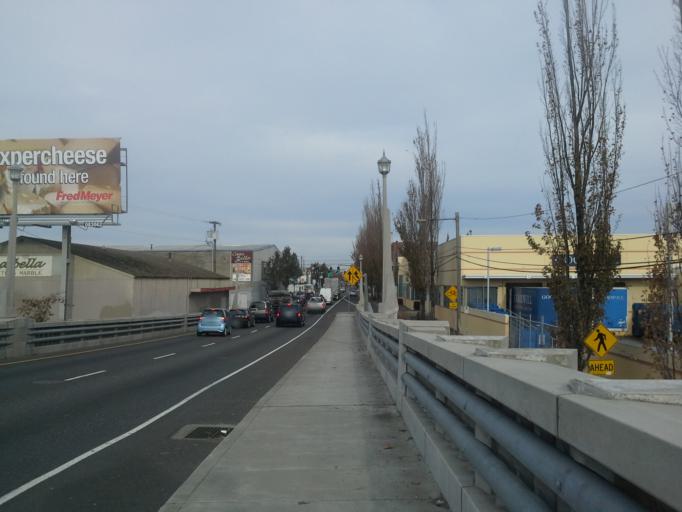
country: US
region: Oregon
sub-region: Multnomah County
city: Portland
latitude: 45.5079
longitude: -122.6608
